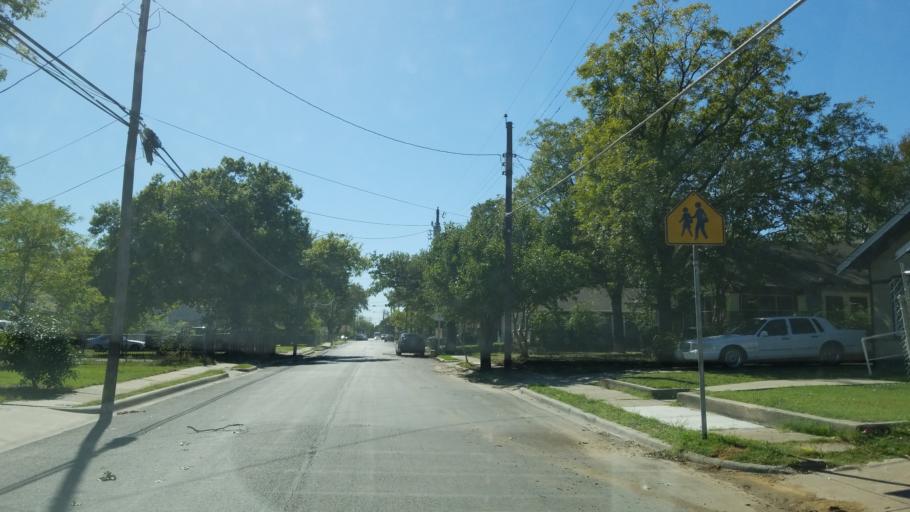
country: US
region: Texas
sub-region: Dallas County
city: Dallas
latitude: 32.7768
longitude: -96.7478
